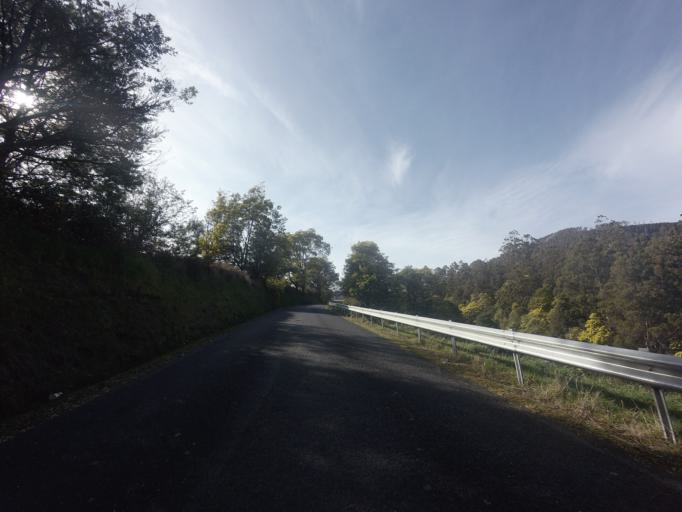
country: AU
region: Tasmania
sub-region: Kingborough
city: Kettering
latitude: -43.1735
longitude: 147.1654
